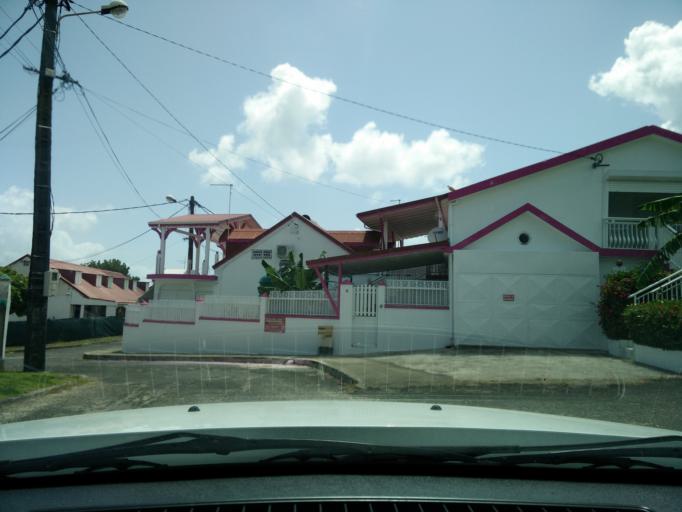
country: GP
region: Guadeloupe
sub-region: Guadeloupe
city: Petit-Canal
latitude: 16.3825
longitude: -61.4874
